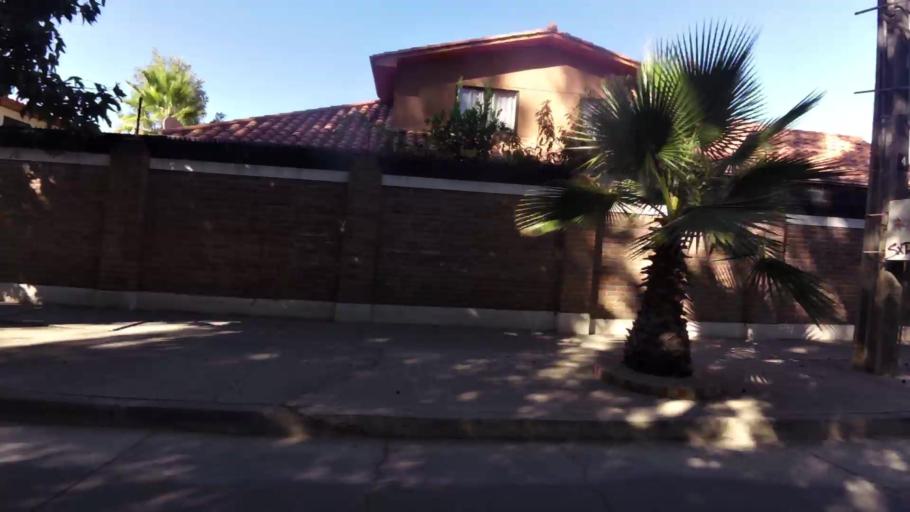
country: CL
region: O'Higgins
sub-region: Provincia de Cachapoal
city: Rancagua
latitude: -34.1892
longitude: -70.7153
